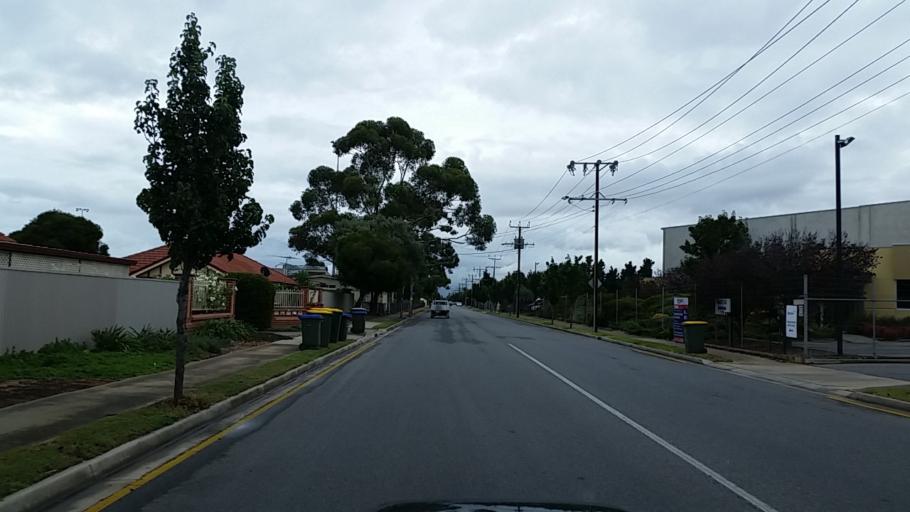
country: AU
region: South Australia
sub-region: Charles Sturt
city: Findon
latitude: -34.8979
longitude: 138.5415
